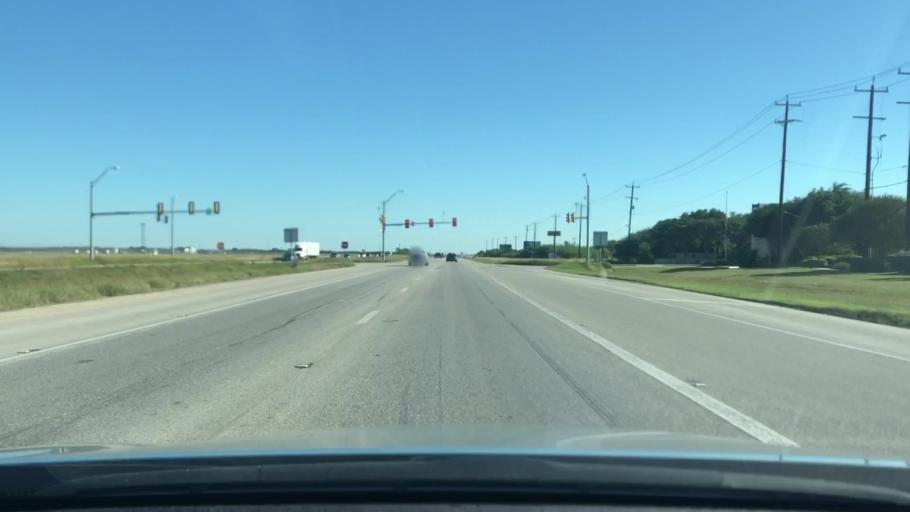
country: US
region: Texas
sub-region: Bexar County
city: Converse
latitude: 29.5225
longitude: -98.2942
